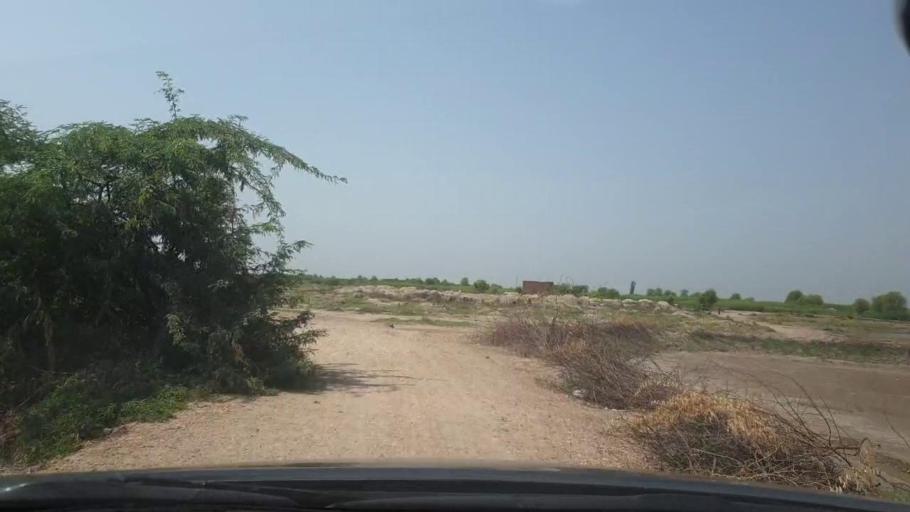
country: PK
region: Sindh
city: Tando Bago
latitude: 24.8035
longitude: 69.1547
